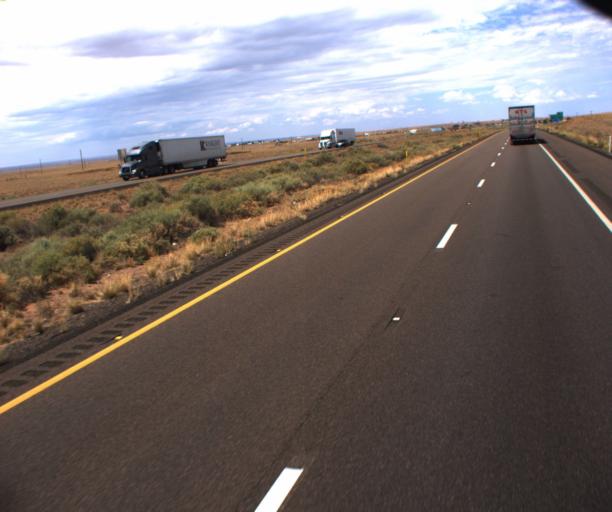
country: US
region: Arizona
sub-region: Navajo County
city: Holbrook
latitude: 34.9833
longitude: -110.0406
